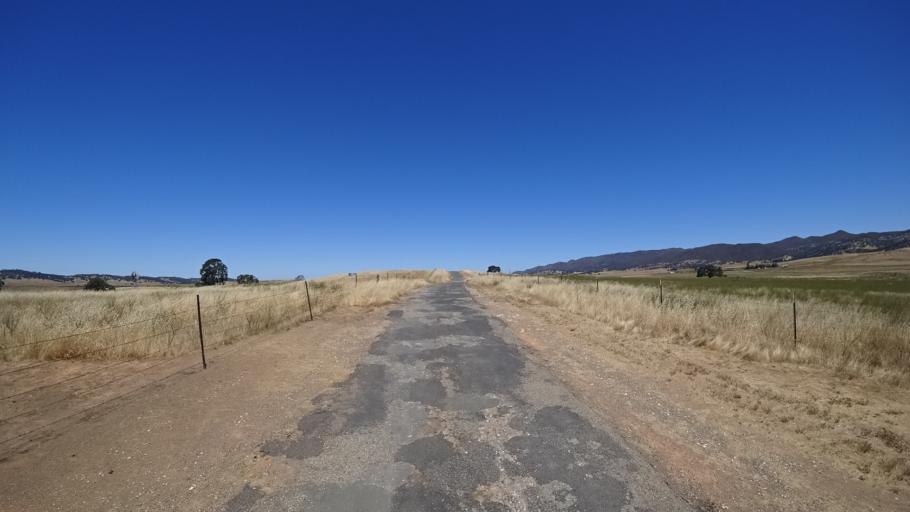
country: US
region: California
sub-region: Calaveras County
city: Copperopolis
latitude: 38.0434
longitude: -120.7320
